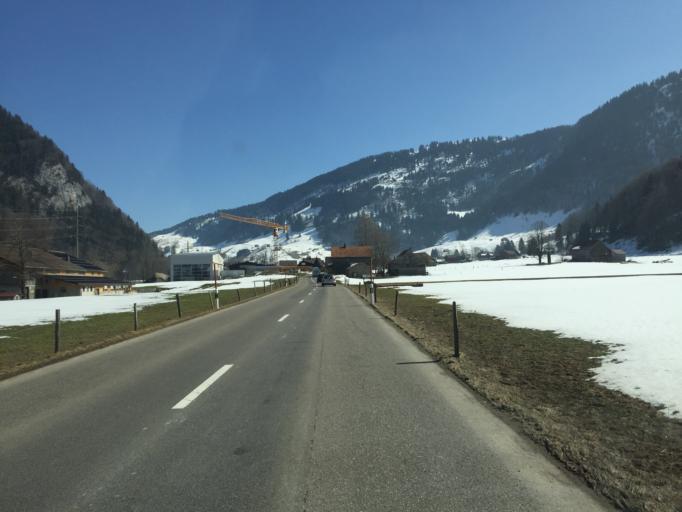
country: CH
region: Saint Gallen
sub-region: Wahlkreis Sarganserland
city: Quarten
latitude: 47.1872
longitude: 9.2437
